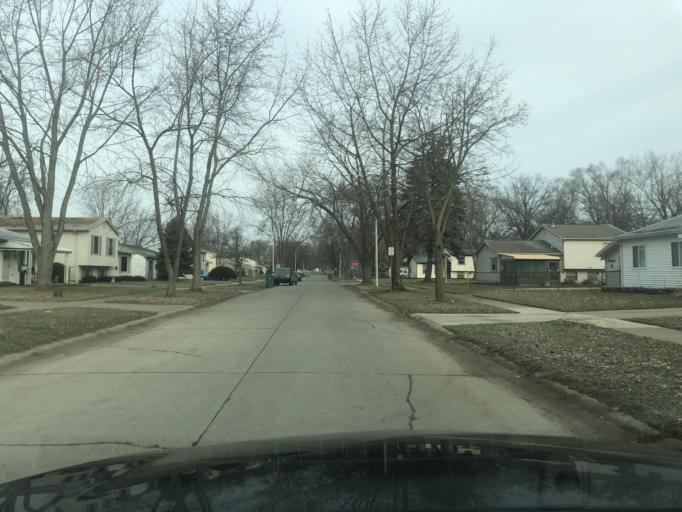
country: US
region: Michigan
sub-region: Wayne County
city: Taylor
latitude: 42.1898
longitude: -83.3146
